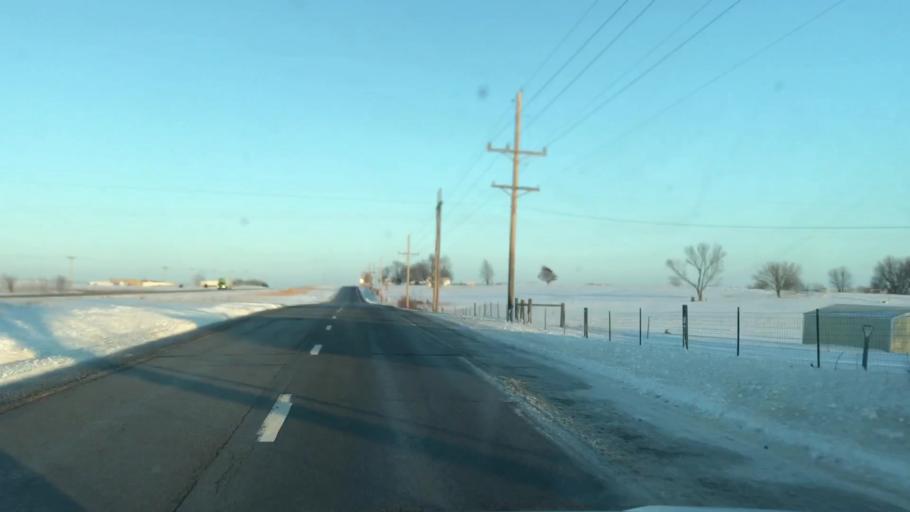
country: US
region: Missouri
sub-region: Clinton County
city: Cameron
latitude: 39.7546
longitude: -94.3092
